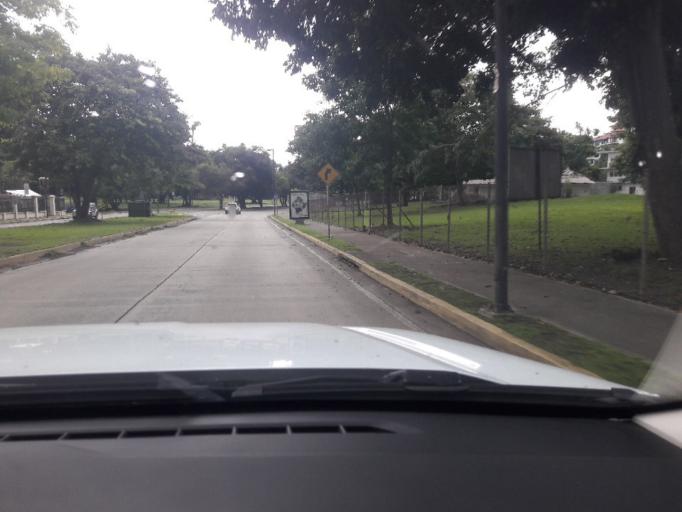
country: PA
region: Panama
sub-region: Distrito de Panama
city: Ancon
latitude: 8.9407
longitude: -79.5509
